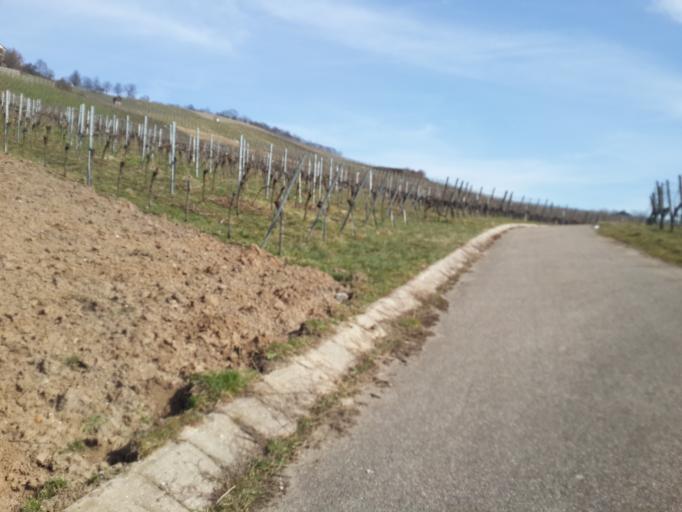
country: DE
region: Baden-Wuerttemberg
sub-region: Regierungsbezirk Stuttgart
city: Heilbronn
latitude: 49.1573
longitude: 9.2302
